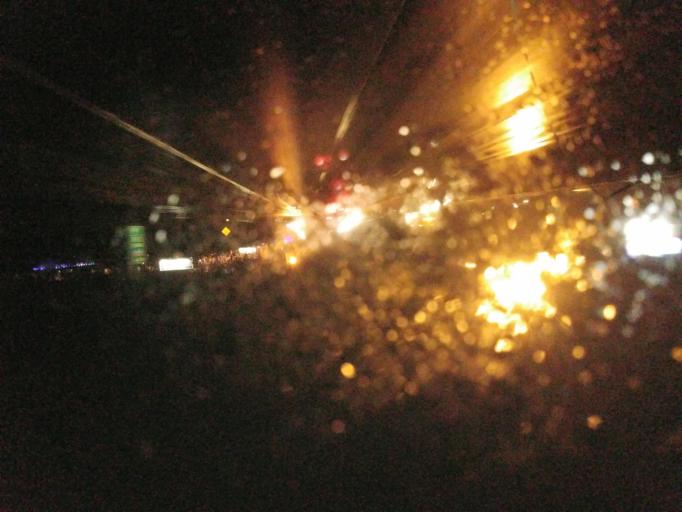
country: US
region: Missouri
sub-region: Saint Louis County
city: Eureka
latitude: 38.5057
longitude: -90.6796
